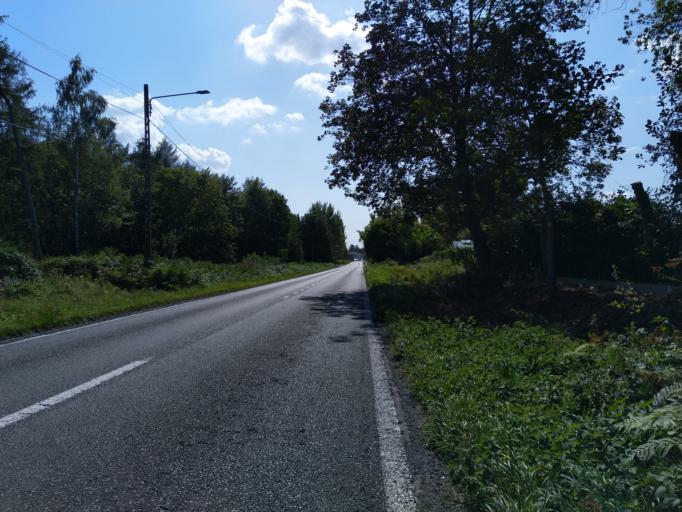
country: BE
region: Wallonia
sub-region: Province du Hainaut
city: Saint-Ghislain
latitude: 50.4983
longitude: 3.8325
